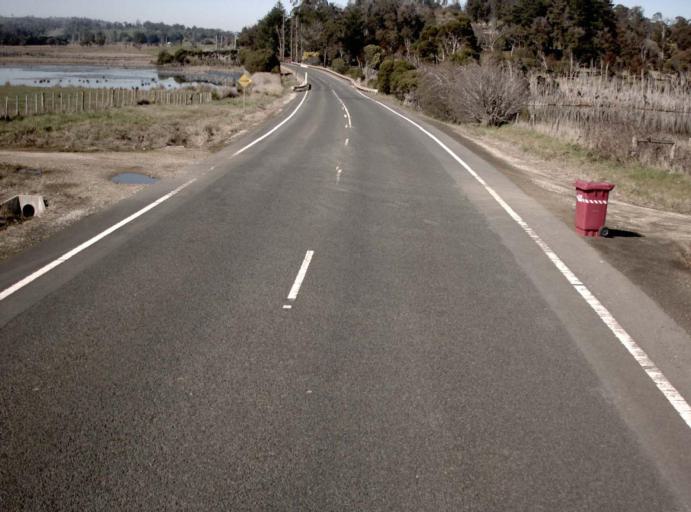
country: AU
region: Tasmania
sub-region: Launceston
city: Mayfield
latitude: -41.3153
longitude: 147.0541
